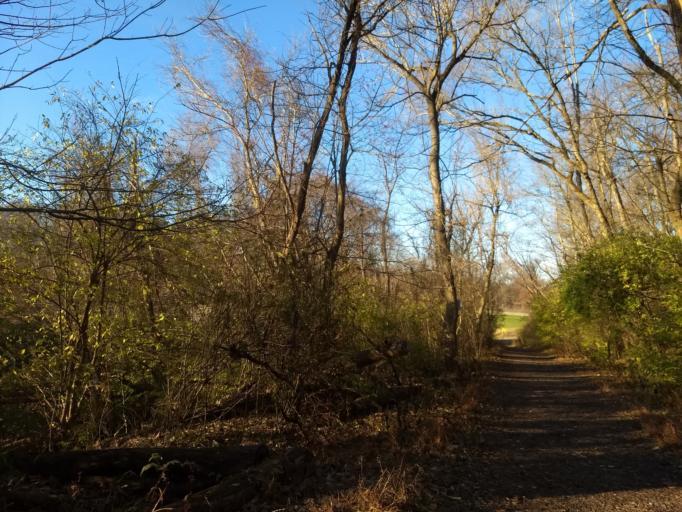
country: US
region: Pennsylvania
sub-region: Allegheny County
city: South Park Township
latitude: 40.3006
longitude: -80.0017
